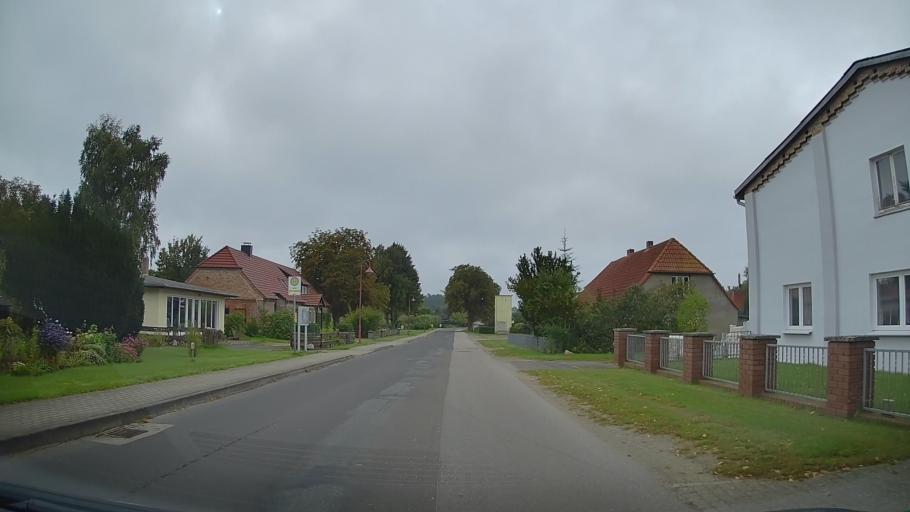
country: DE
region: Mecklenburg-Vorpommern
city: Kavelstorf
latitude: 53.9466
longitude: 12.2142
